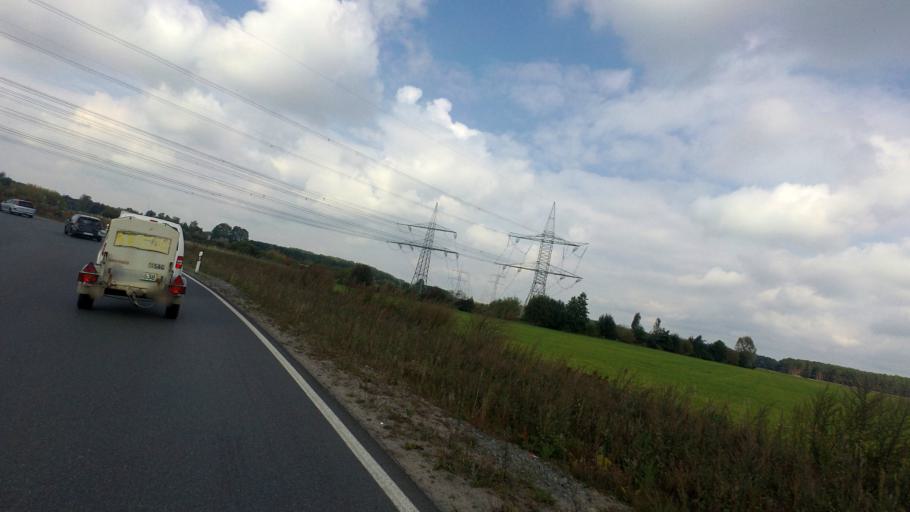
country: DE
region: Brandenburg
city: Bad Liebenwerda
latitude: 51.5140
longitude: 13.4295
